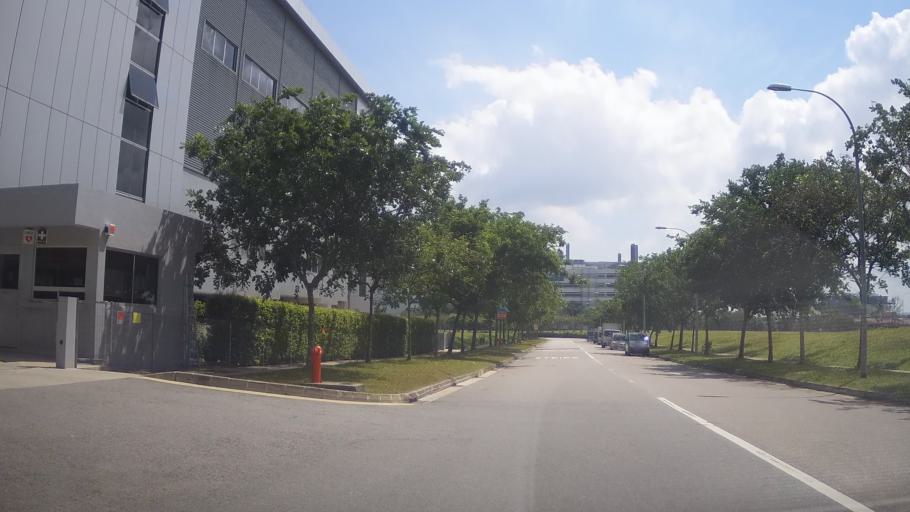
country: SG
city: Singapore
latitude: 1.3239
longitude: 103.7159
